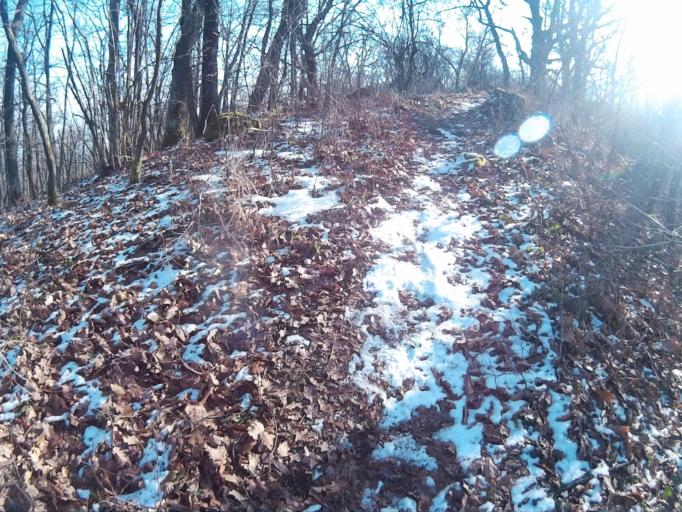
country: HU
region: Nograd
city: Paszto
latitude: 47.9652
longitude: 19.6458
